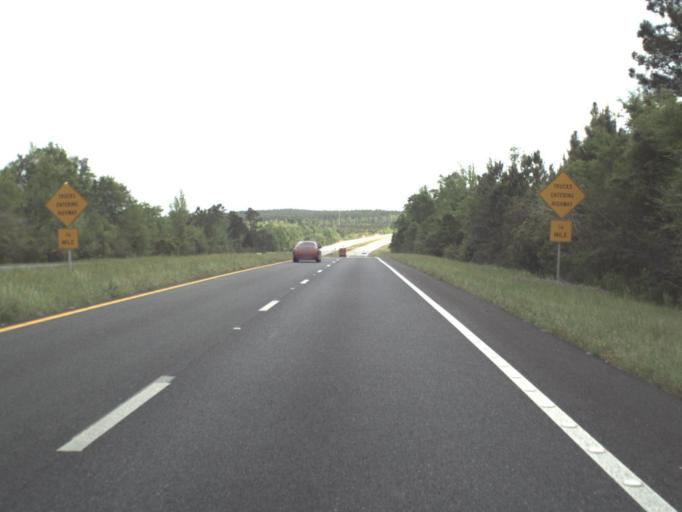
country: US
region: Florida
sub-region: Escambia County
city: Molino
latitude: 30.8006
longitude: -87.3356
